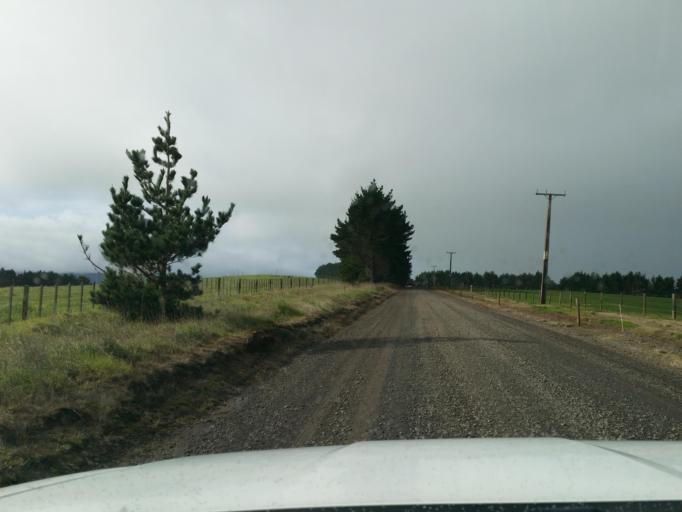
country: NZ
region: Northland
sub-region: Kaipara District
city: Dargaville
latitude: -35.7549
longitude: 173.6073
